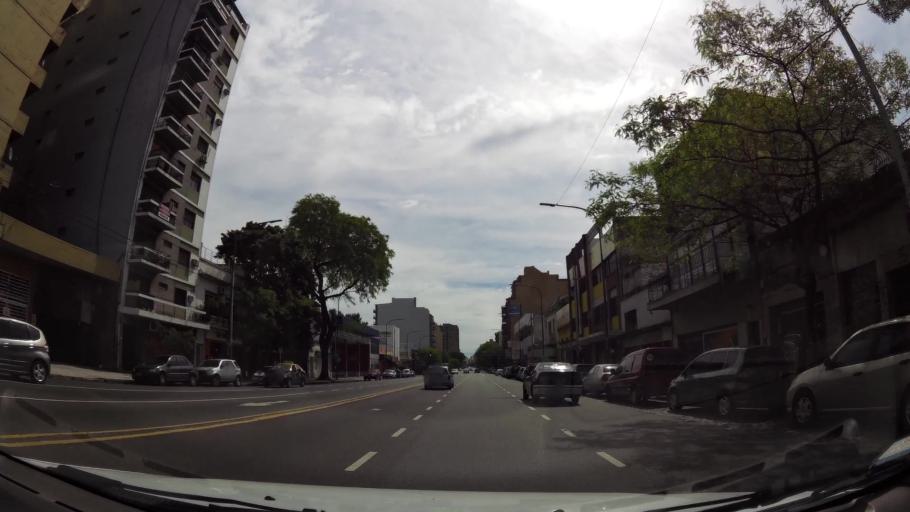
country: AR
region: Buenos Aires F.D.
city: Villa Santa Rita
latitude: -34.6371
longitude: -58.4967
